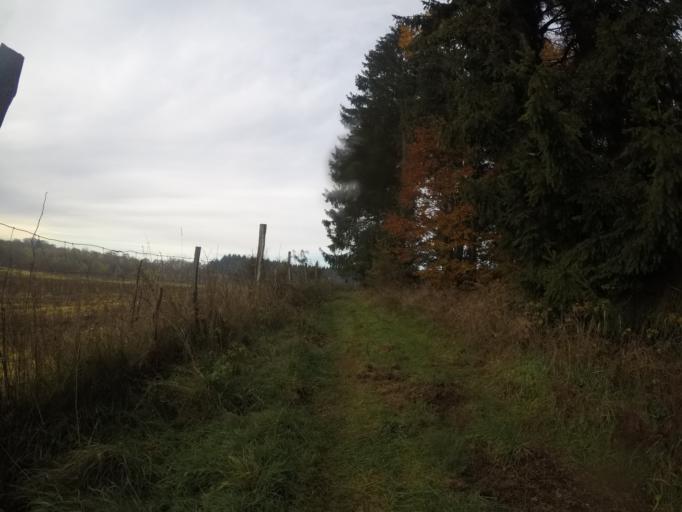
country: BE
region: Wallonia
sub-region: Province du Luxembourg
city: Habay-la-Vieille
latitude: 49.7356
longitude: 5.5998
